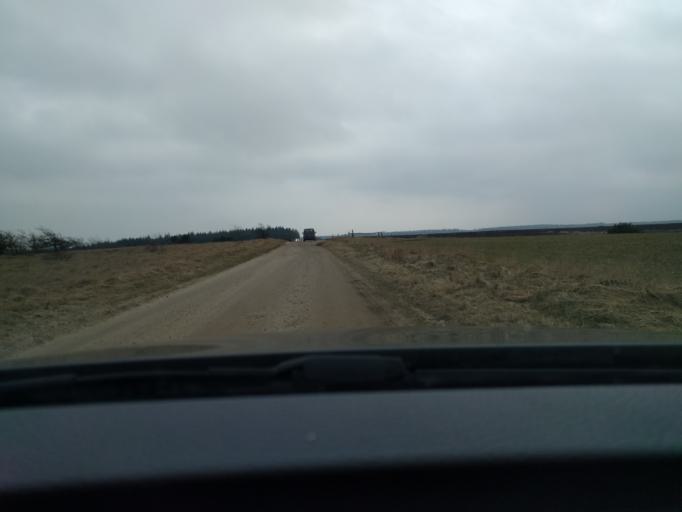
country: DK
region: Central Jutland
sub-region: Skive Kommune
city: Skive
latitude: 56.5114
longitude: 8.9485
